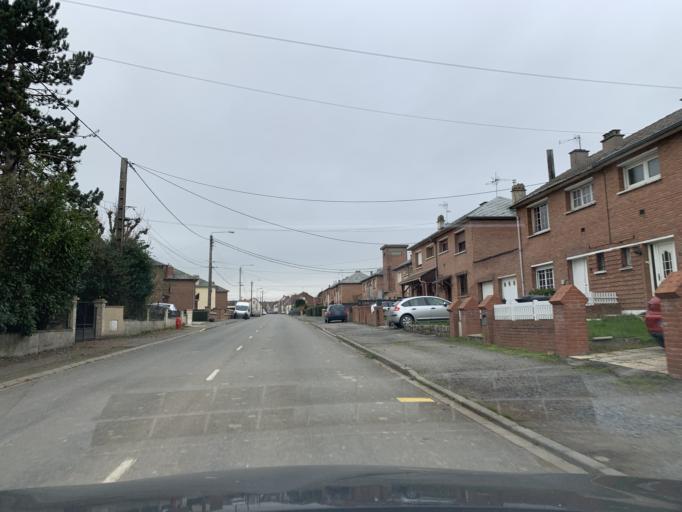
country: FR
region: Nord-Pas-de-Calais
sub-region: Departement du Pas-de-Calais
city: Oisy-le-Verger
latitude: 50.2476
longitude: 3.1295
